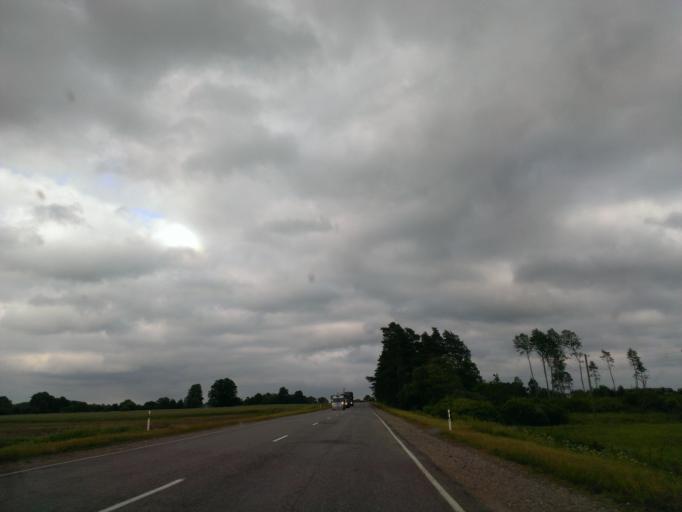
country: LV
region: Skrunda
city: Skrunda
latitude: 56.6775
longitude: 22.2052
